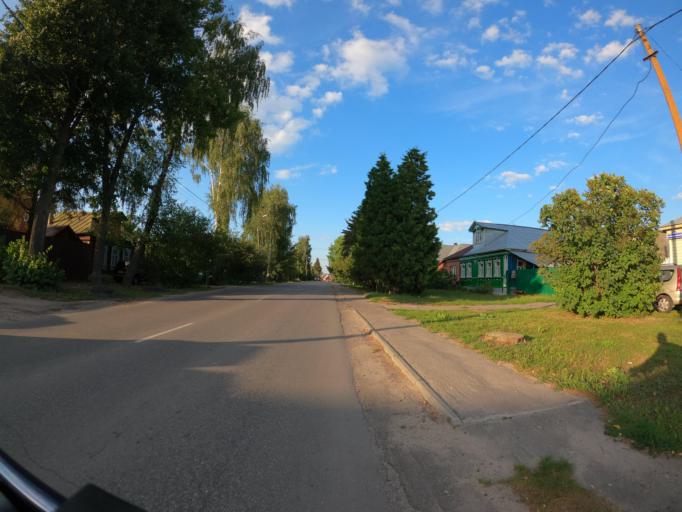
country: RU
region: Moskovskaya
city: Raduzhnyy
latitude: 55.1042
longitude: 38.7363
